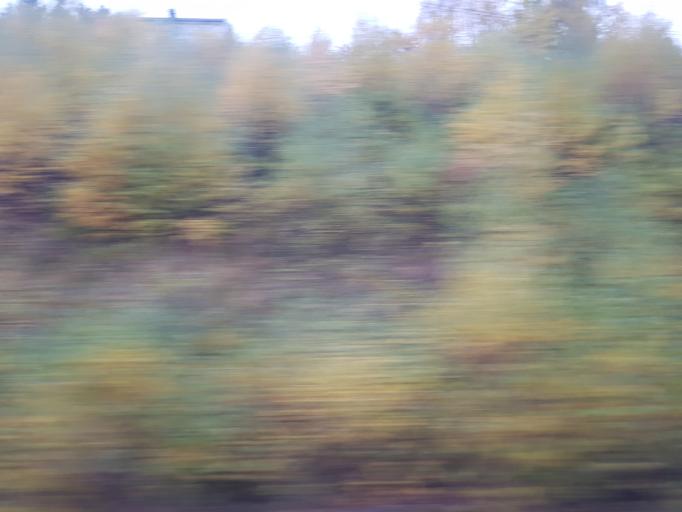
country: NO
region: Oppland
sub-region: Sel
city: Otta
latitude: 61.8435
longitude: 9.4042
